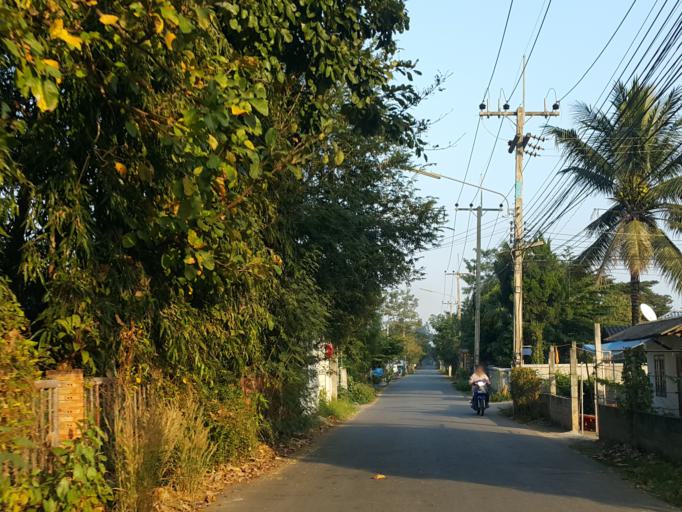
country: TH
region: Chiang Mai
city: Chiang Mai
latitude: 18.9087
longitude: 98.9072
